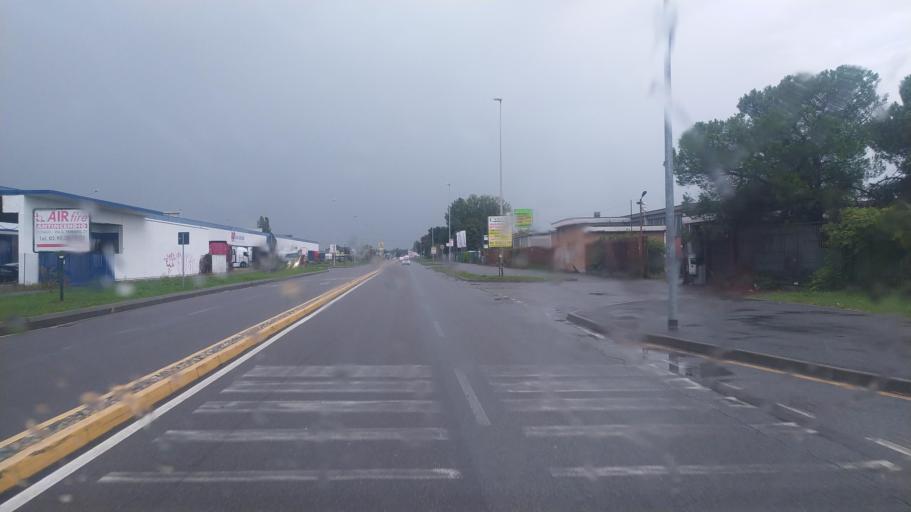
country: IT
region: Lombardy
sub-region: Citta metropolitana di Milano
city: Cusago
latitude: 45.4366
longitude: 9.0469
